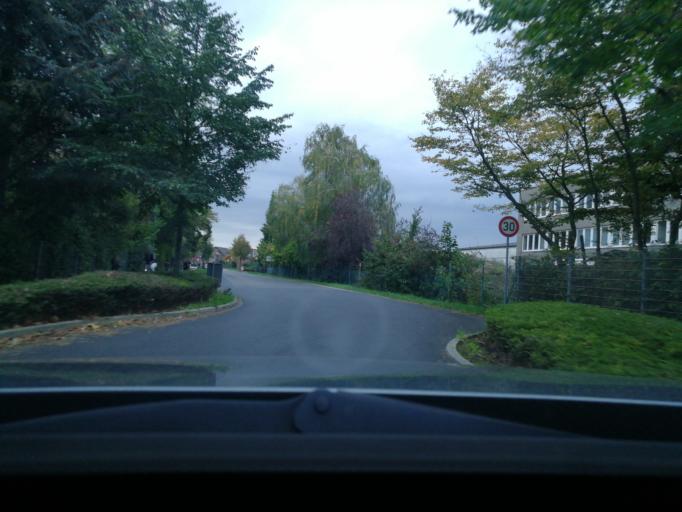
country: DE
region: North Rhine-Westphalia
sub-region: Regierungsbezirk Dusseldorf
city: Neuss
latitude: 51.1376
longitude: 6.7488
